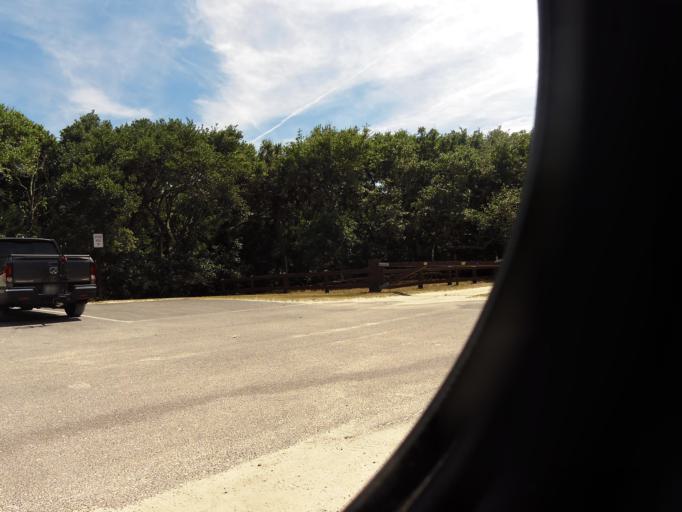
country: US
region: Florida
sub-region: Saint Johns County
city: Villano Beach
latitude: 30.0224
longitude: -81.3324
